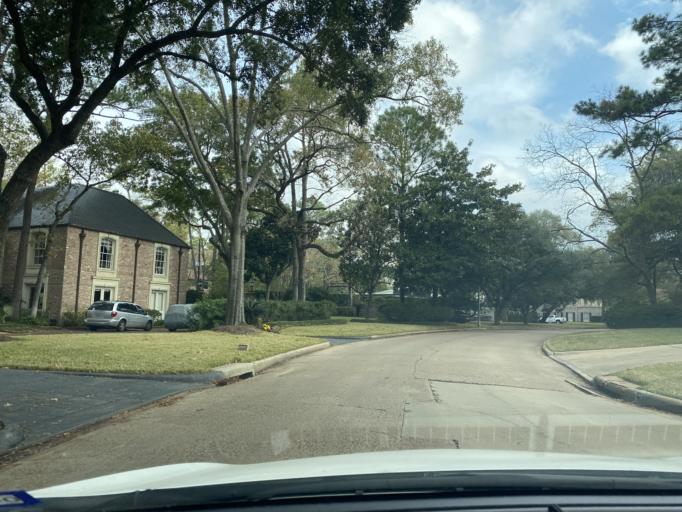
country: US
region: Texas
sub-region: Harris County
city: Hunters Creek Village
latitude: 29.7696
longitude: -95.4765
